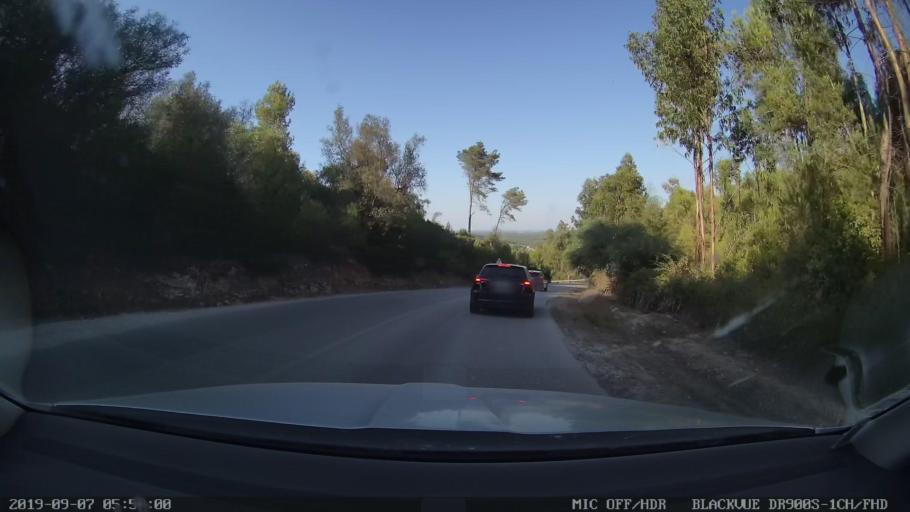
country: PT
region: Setubal
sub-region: Sesimbra
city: Sesimbra
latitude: 38.4623
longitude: -9.0960
